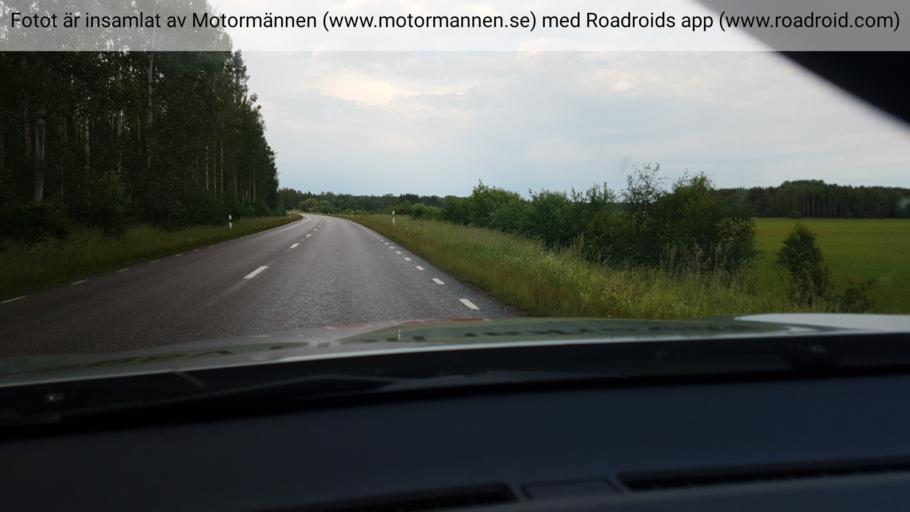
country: SE
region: Vaestra Goetaland
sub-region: Hjo Kommun
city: Hjo
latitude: 58.2373
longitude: 14.2242
